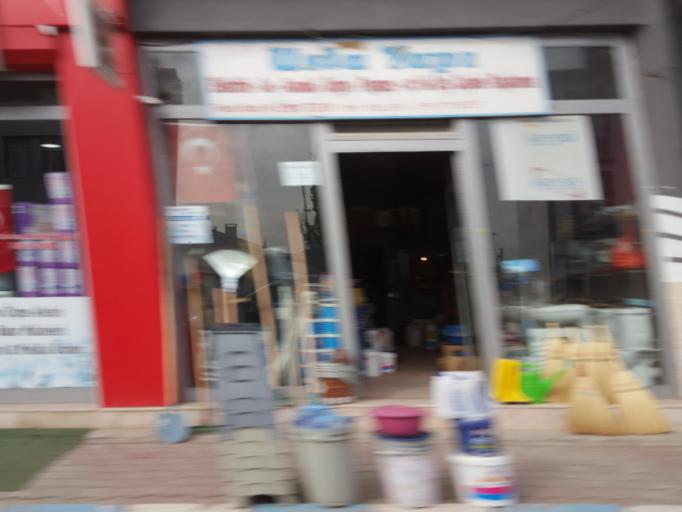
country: TR
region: Kirikkale
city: Bahsili
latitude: 39.8129
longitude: 33.4716
